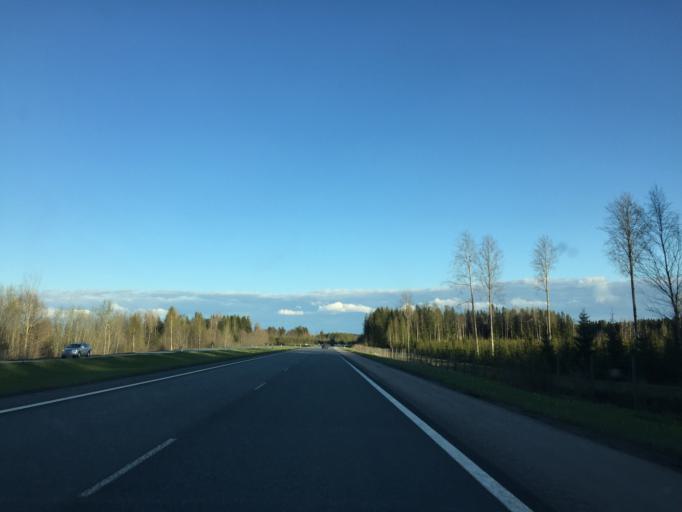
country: FI
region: Haeme
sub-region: Haemeenlinna
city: Tervakoski
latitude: 60.7848
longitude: 24.7030
